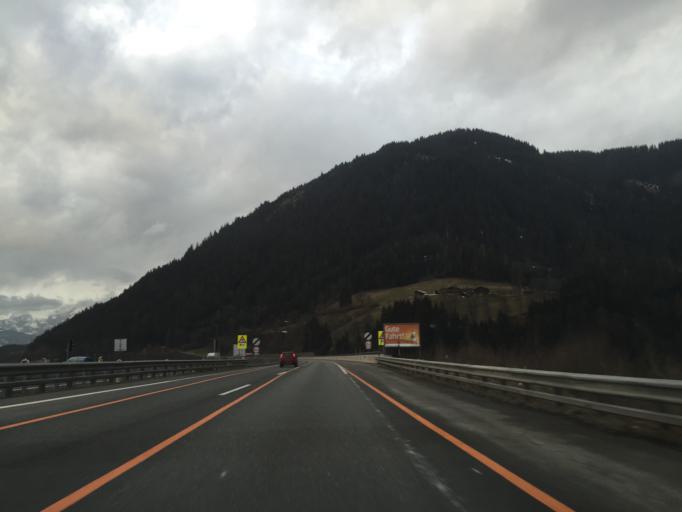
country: AT
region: Salzburg
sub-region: Politischer Bezirk Sankt Johann im Pongau
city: Huttau
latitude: 47.4264
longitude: 13.2977
